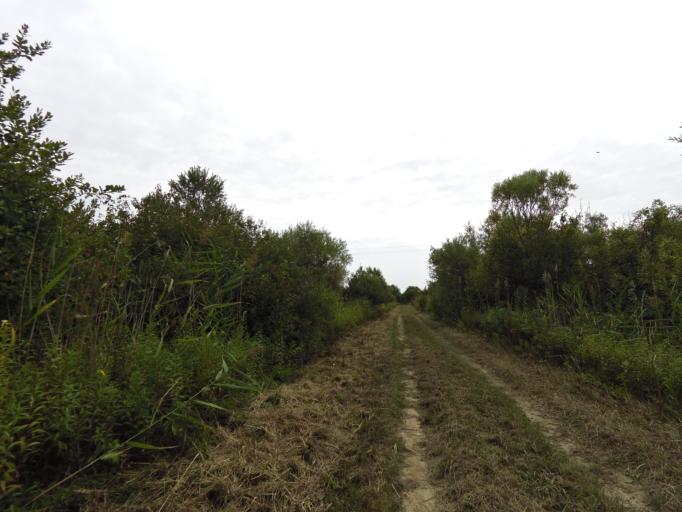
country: HU
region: Veszprem
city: Tapolca
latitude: 46.8343
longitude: 17.3688
